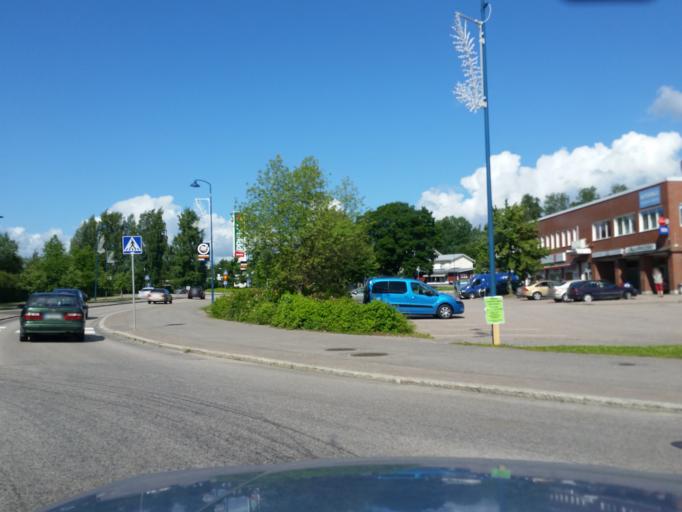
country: FI
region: Uusimaa
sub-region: Helsinki
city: Vihti
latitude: 60.3322
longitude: 24.3272
